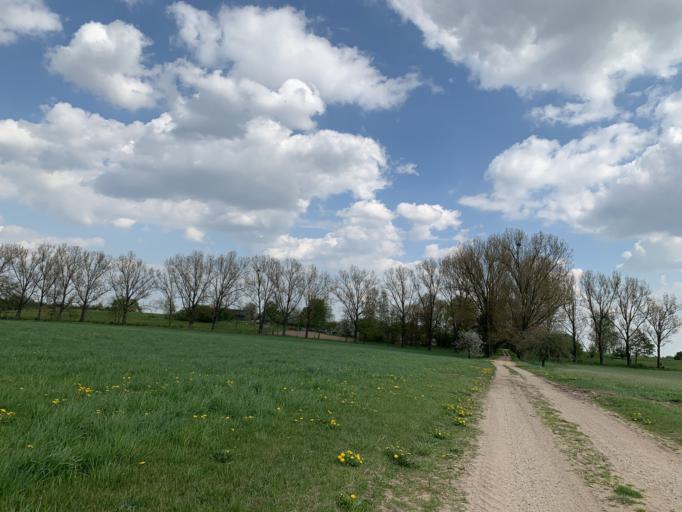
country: BY
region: Minsk
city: Nyasvizh
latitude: 53.2446
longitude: 26.6934
